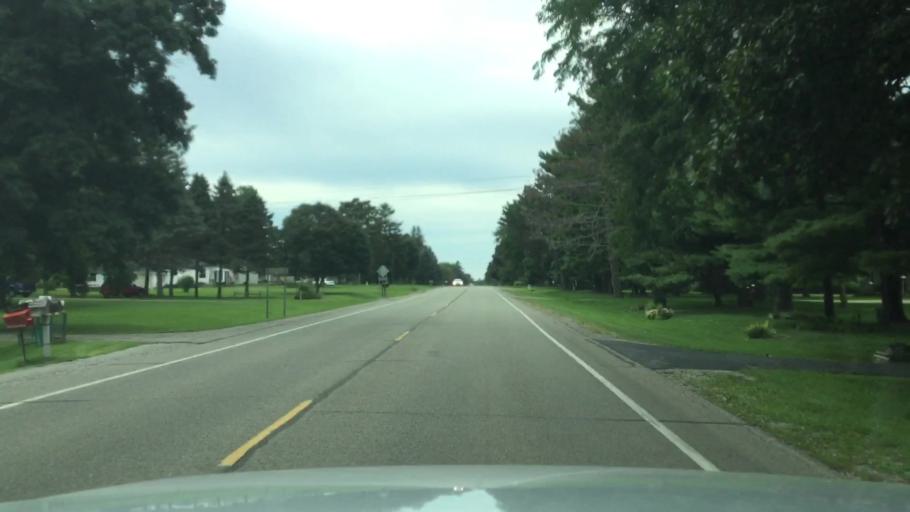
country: US
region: Michigan
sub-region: Shiawassee County
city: Durand
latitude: 42.9328
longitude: -83.9500
